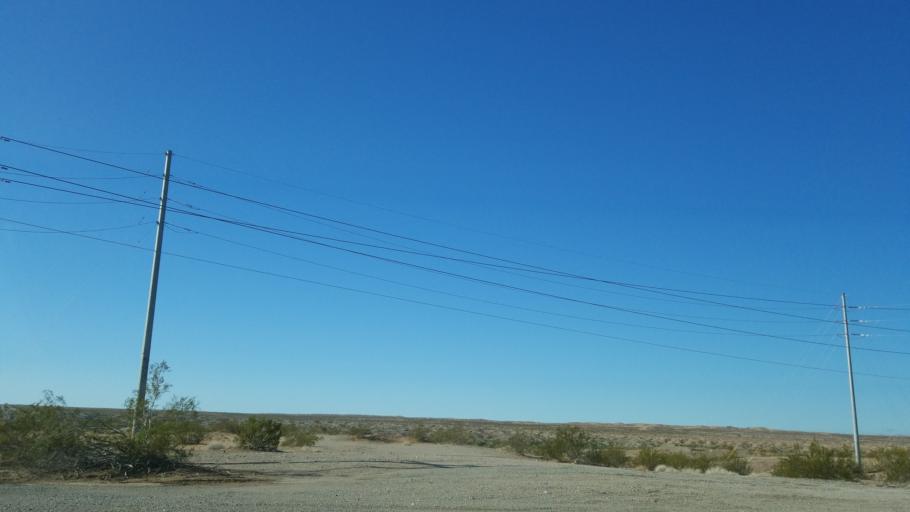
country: US
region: Arizona
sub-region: La Paz County
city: Parker
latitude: 33.9974
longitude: -114.2167
